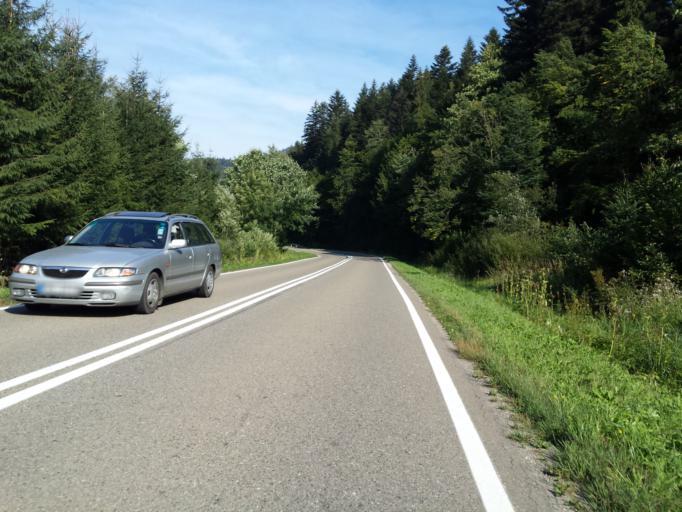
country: PL
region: Subcarpathian Voivodeship
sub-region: Powiat leski
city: Baligrod
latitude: 49.2881
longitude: 22.2726
